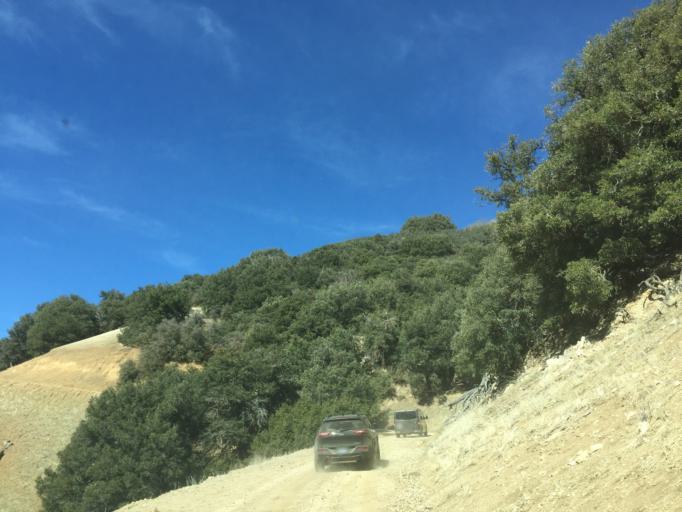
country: US
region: California
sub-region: Kern County
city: Stallion Springs
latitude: 34.9205
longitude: -118.6648
